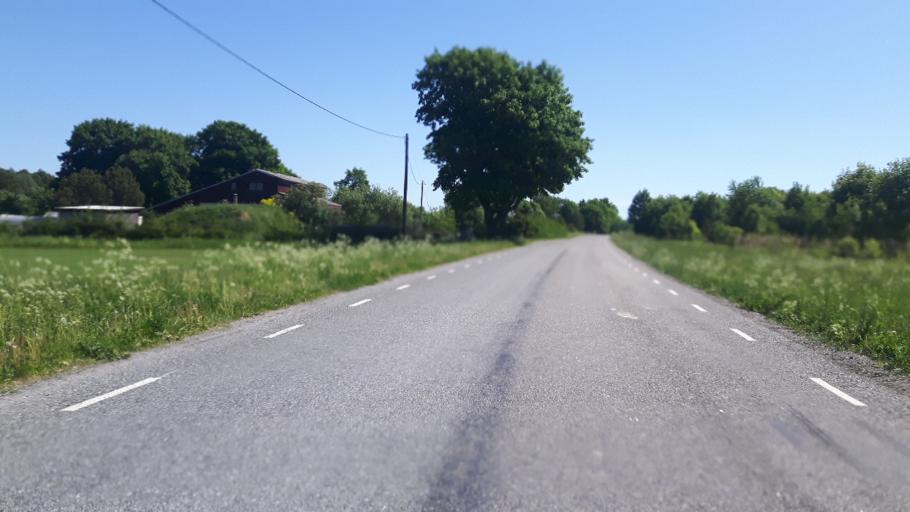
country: EE
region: Raplamaa
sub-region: Kohila vald
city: Kohila
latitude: 59.1899
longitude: 24.7087
